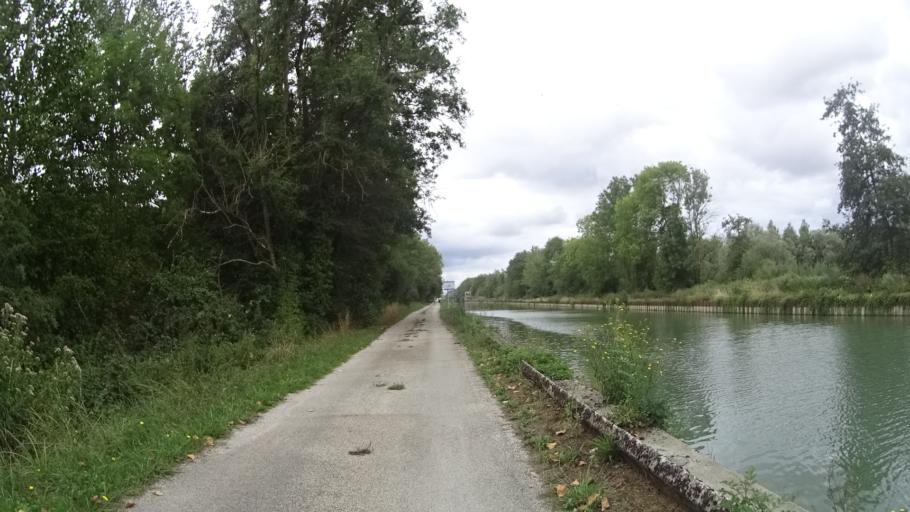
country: FR
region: Picardie
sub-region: Departement de l'Aisne
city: La Fere
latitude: 49.6972
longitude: 3.3705
